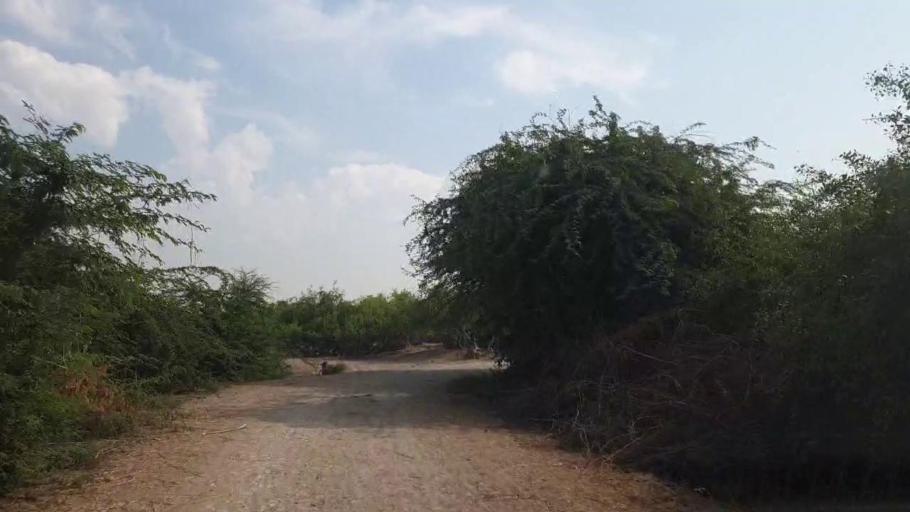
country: PK
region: Sindh
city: Tando Bago
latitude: 24.9352
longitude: 69.0011
